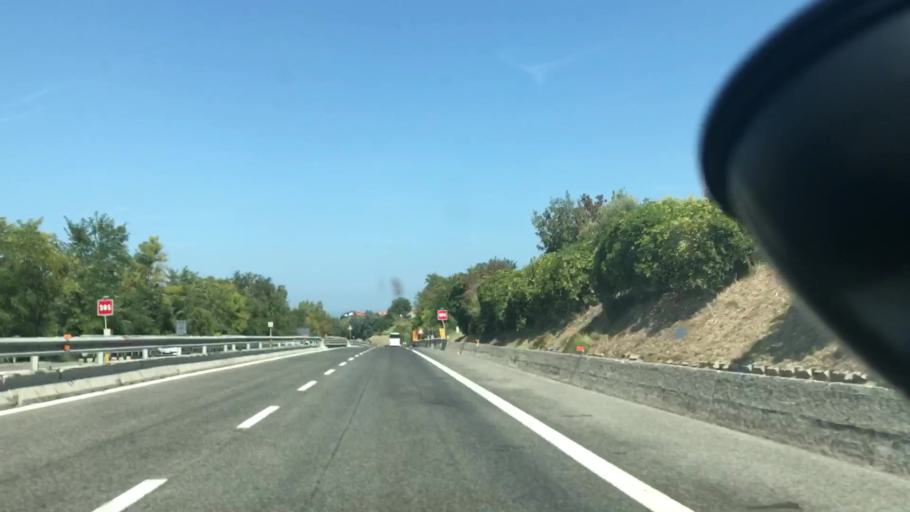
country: IT
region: Abruzzo
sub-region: Provincia di Chieti
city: San Vito Chietino
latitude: 42.3055
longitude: 14.4221
